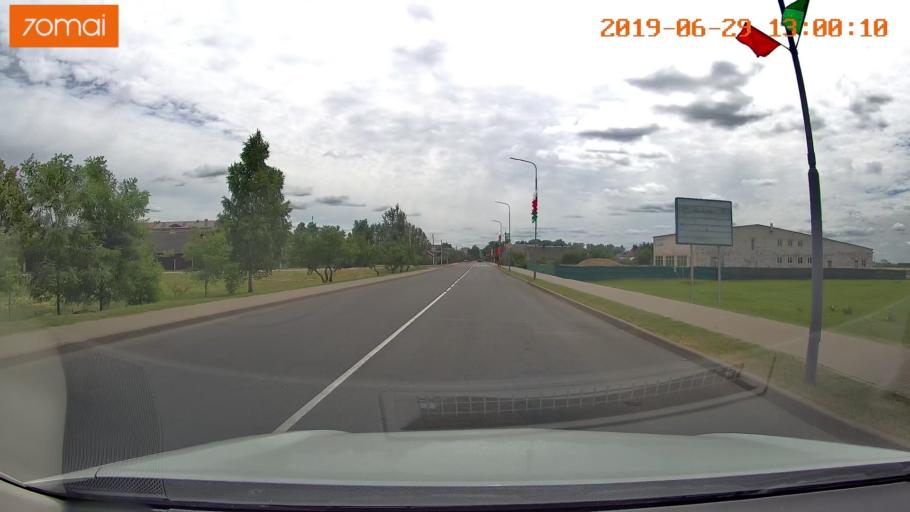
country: BY
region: Minsk
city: Slutsk
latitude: 53.0467
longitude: 27.5559
